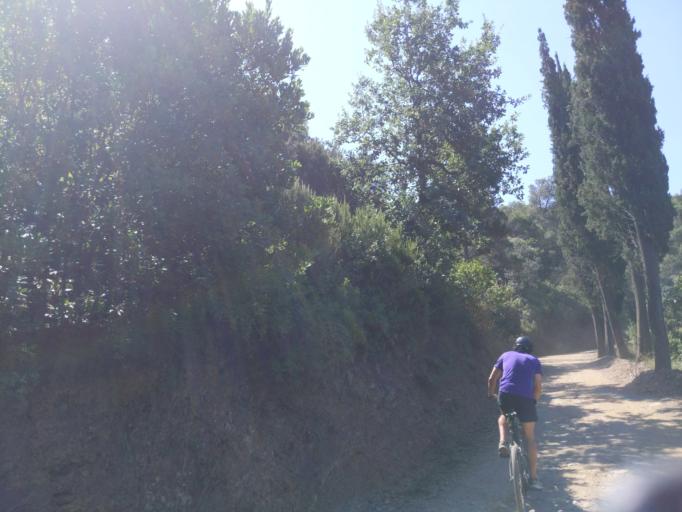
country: ES
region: Catalonia
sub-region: Provincia de Barcelona
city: Nou Barris
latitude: 41.4521
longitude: 2.1545
